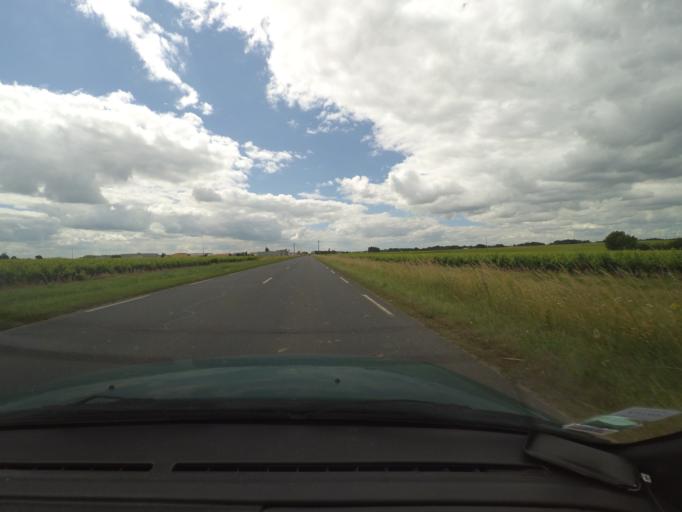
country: FR
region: Pays de la Loire
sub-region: Departement de la Loire-Atlantique
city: Mouzillon
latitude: 47.1301
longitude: -1.2826
